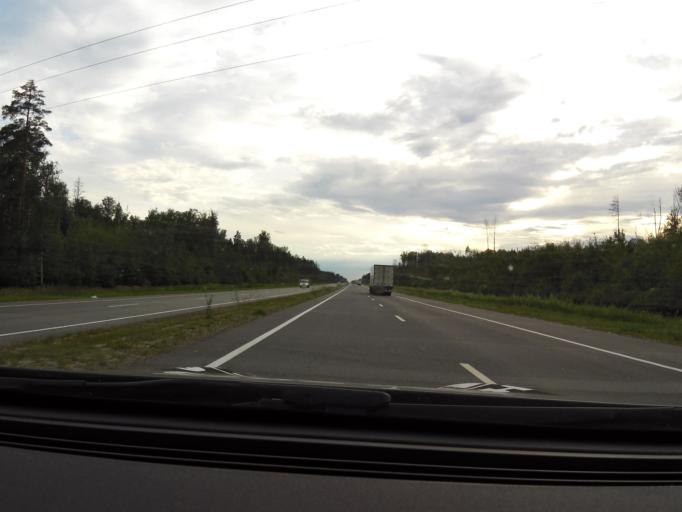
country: RU
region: Vladimir
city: Orgtrud
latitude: 56.0965
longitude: 40.5645
